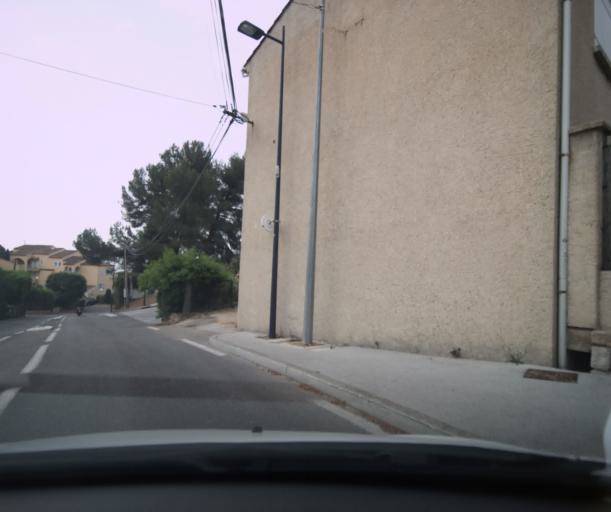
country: FR
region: Provence-Alpes-Cote d'Azur
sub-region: Departement du Var
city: Carqueiranne
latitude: 43.0998
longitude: 6.0796
